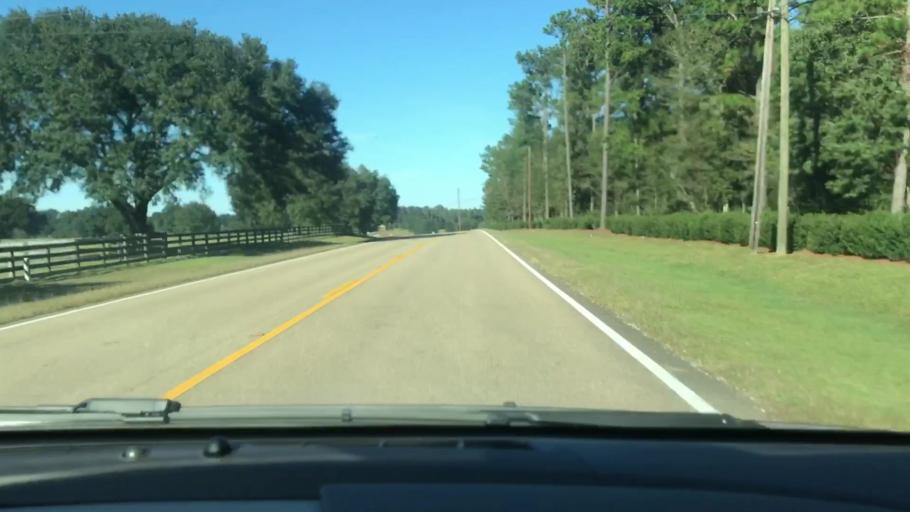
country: US
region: Louisiana
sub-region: Saint Tammany Parish
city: Abita Springs
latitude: 30.5983
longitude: -90.0300
